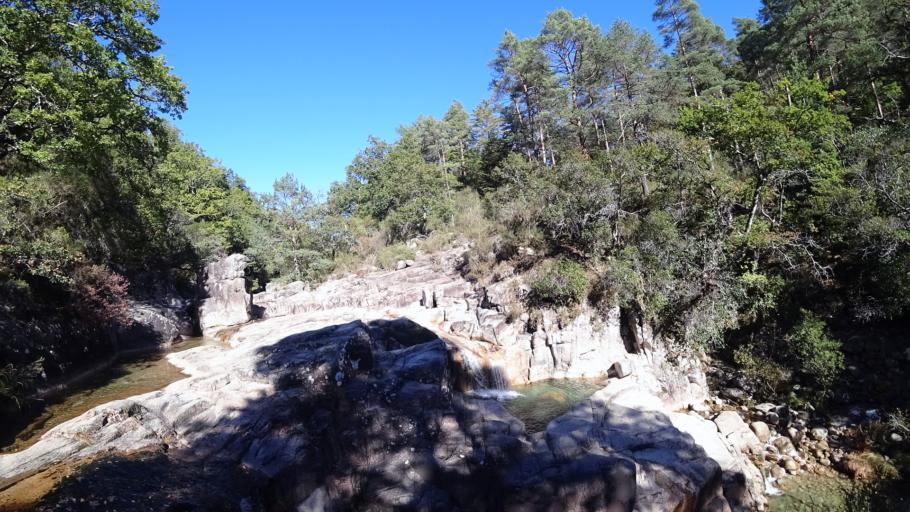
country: ES
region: Galicia
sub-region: Provincia de Ourense
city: Lobios
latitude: 41.7955
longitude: -8.1359
